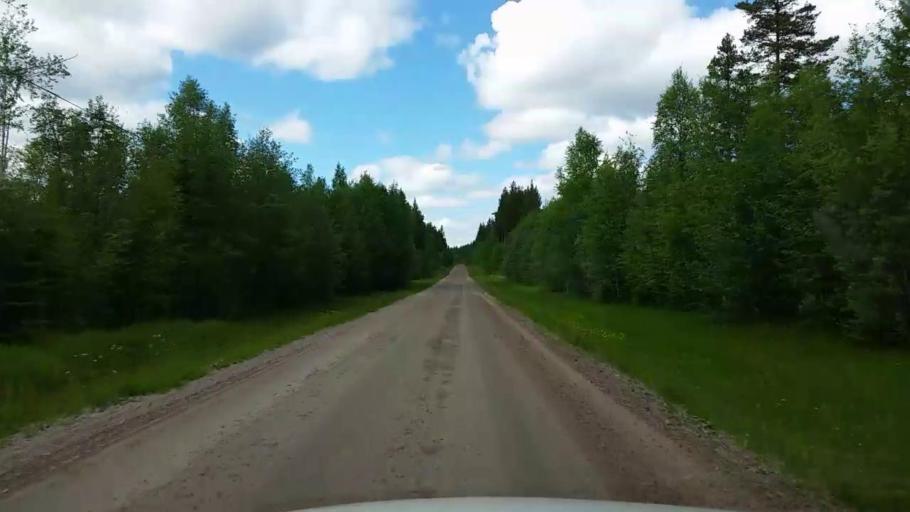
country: SE
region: Gaevleborg
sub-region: Ovanakers Kommun
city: Alfta
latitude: 61.4886
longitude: 15.9867
